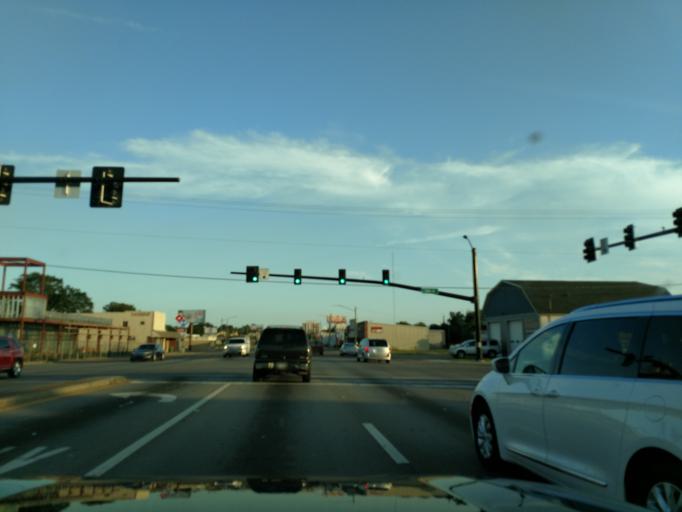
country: US
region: Mississippi
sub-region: Harrison County
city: Gulfport
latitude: 30.3844
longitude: -89.0932
